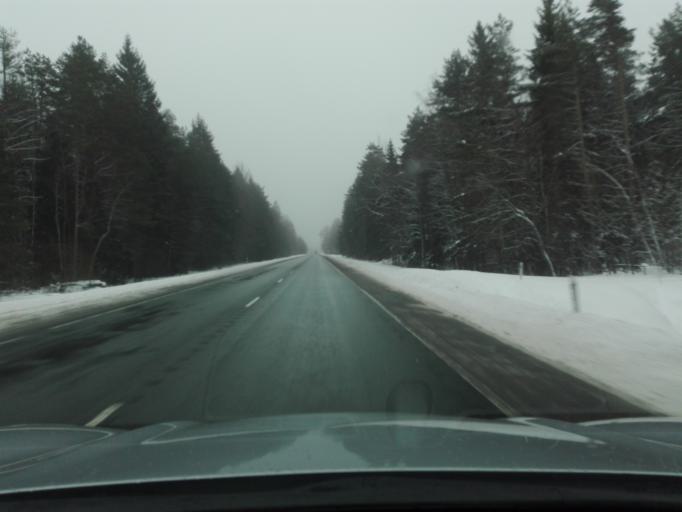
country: EE
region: Raplamaa
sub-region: Kohila vald
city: Kohila
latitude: 59.1540
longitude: 24.7789
